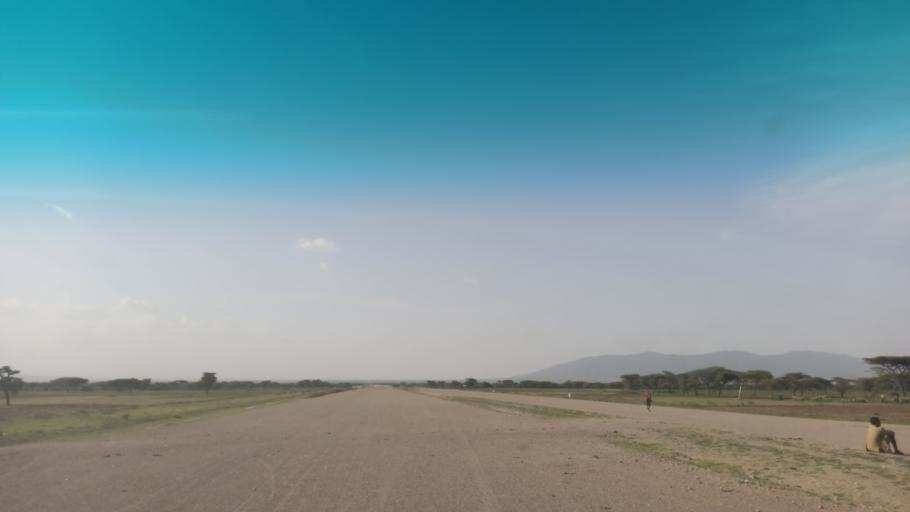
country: ET
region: Oromiya
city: Ziway
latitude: 7.6462
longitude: 38.6822
